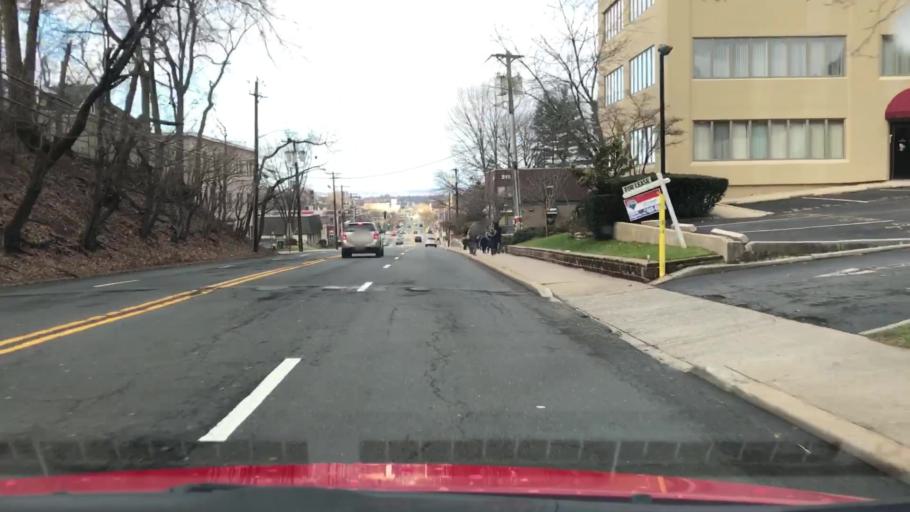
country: US
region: New Jersey
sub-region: Bergen County
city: Teaneck
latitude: 40.8872
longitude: -74.0163
